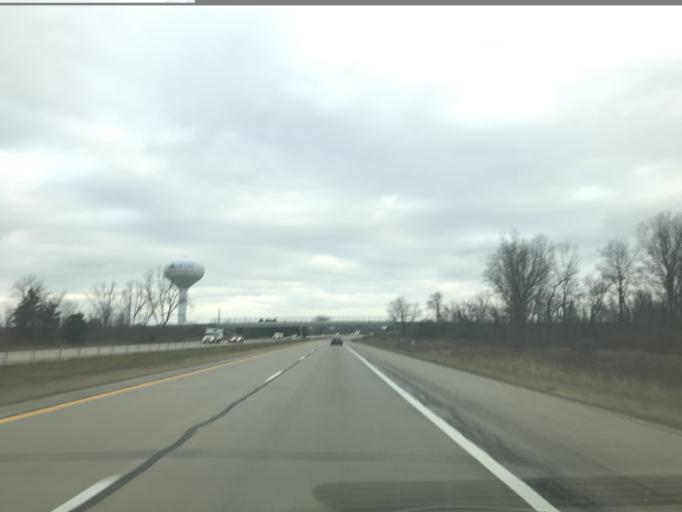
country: US
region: Michigan
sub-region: Eaton County
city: Dimondale
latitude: 42.6950
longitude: -84.6689
